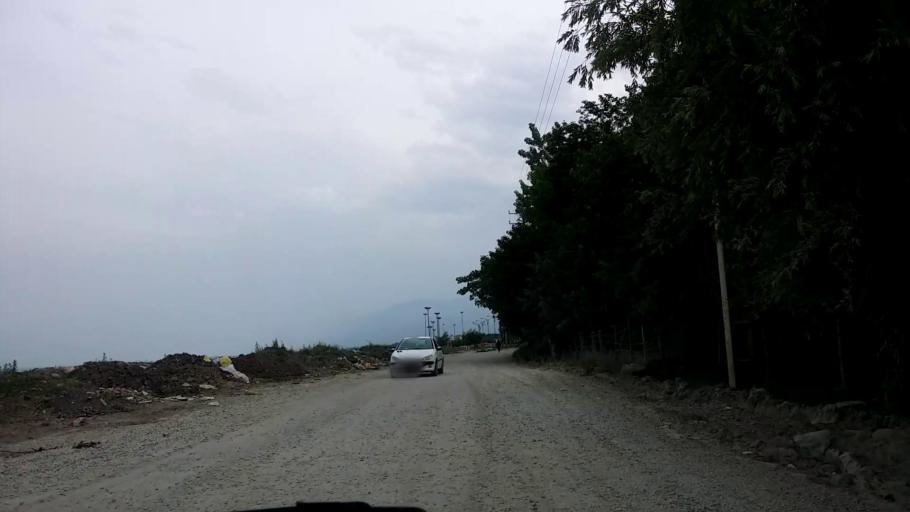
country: IR
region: Mazandaran
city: Chalus
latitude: 36.6833
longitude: 51.4333
